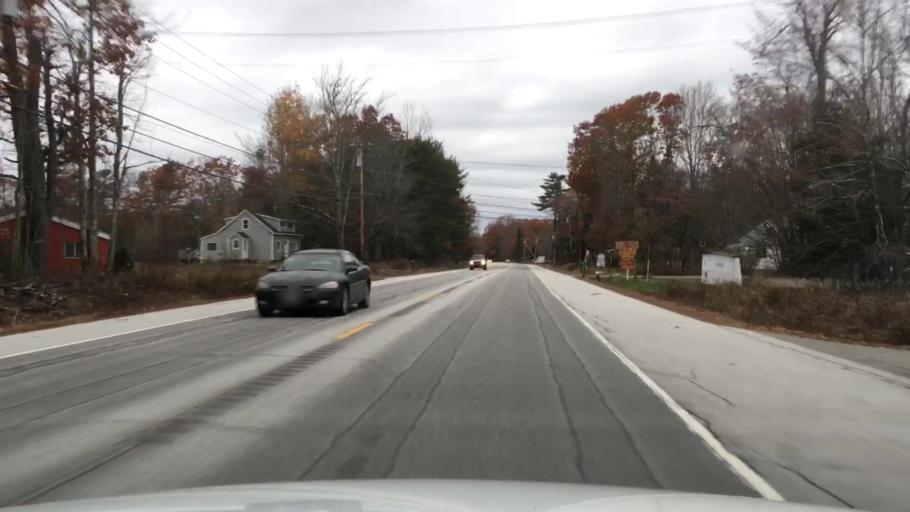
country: US
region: Maine
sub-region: Hancock County
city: Orland
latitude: 44.5639
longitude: -68.7150
